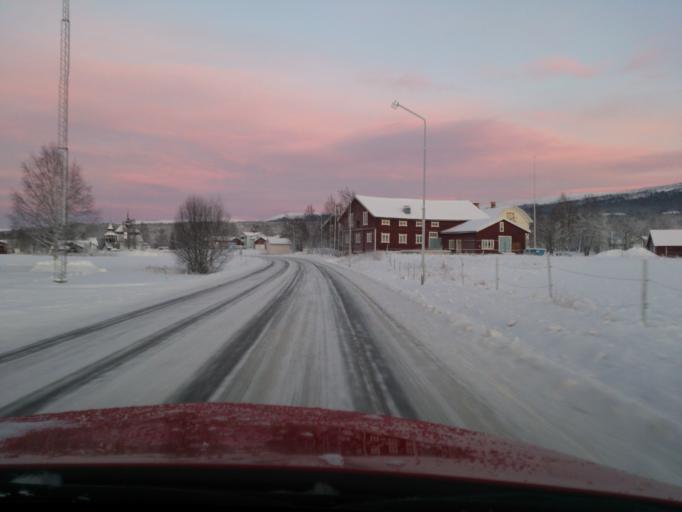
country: SE
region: Jaemtland
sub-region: Harjedalens Kommun
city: Sveg
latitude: 62.4424
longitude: 13.8585
